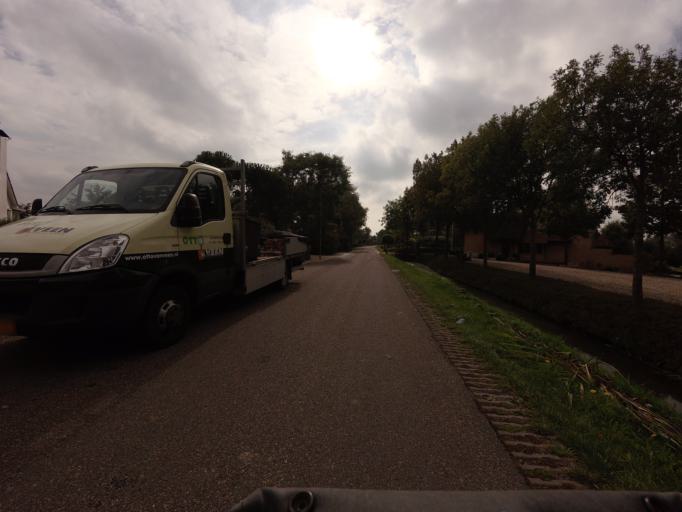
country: NL
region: South Holland
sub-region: Gemeente Giessenlanden
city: Giessenburg
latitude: 51.8874
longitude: 4.8564
